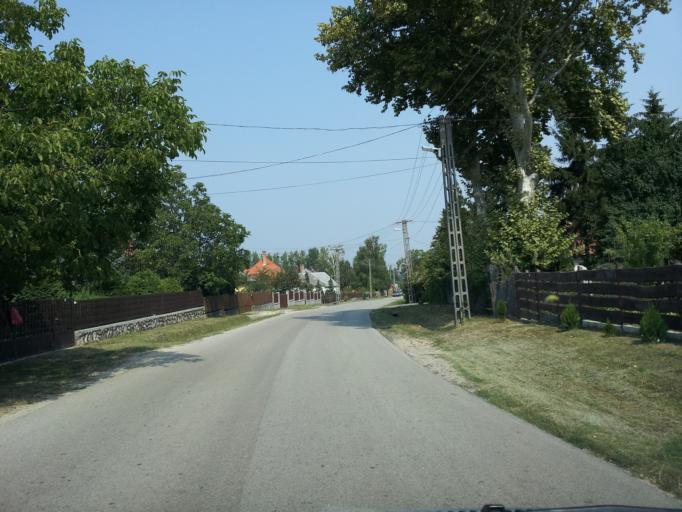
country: HU
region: Gyor-Moson-Sopron
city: Bakonyszentlaszlo
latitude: 47.3929
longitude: 17.8032
